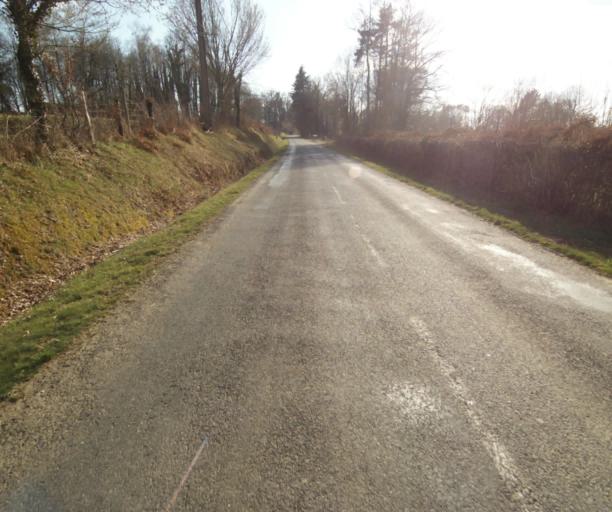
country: FR
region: Limousin
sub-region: Departement de la Correze
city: Saint-Mexant
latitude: 45.3359
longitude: 1.6149
